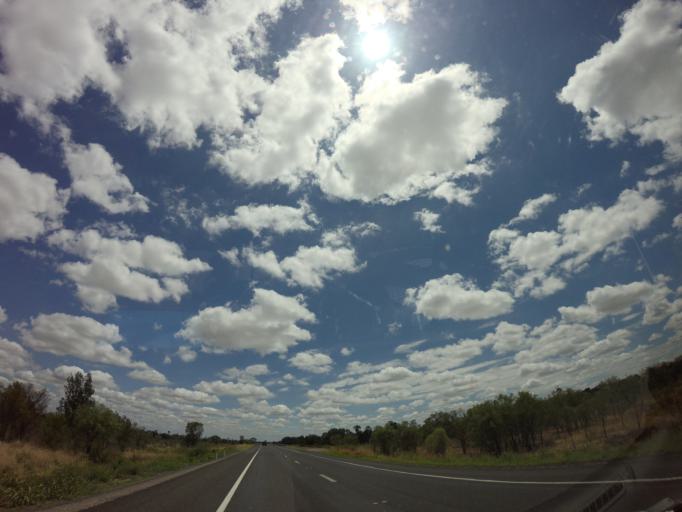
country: AU
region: New South Wales
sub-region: Moree Plains
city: Boggabilla
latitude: -29.0066
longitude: 150.0658
